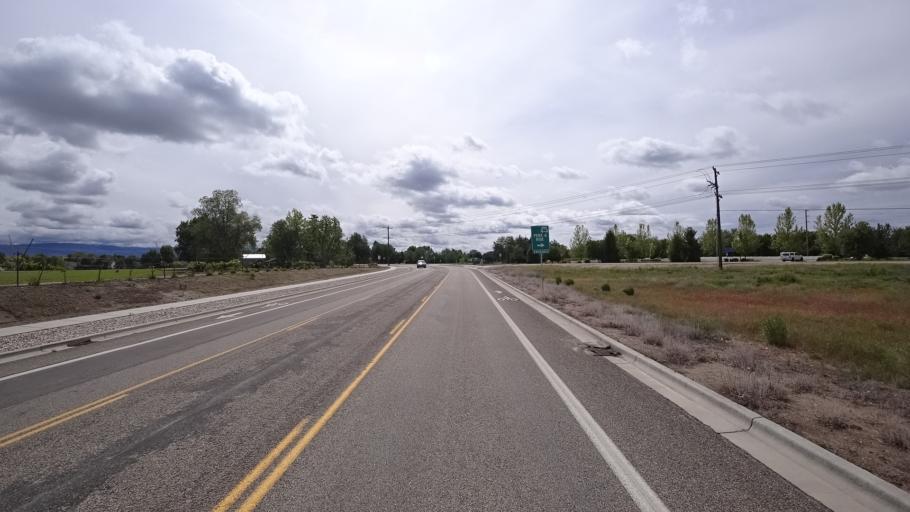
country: US
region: Idaho
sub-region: Ada County
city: Eagle
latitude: 43.6962
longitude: -116.3781
